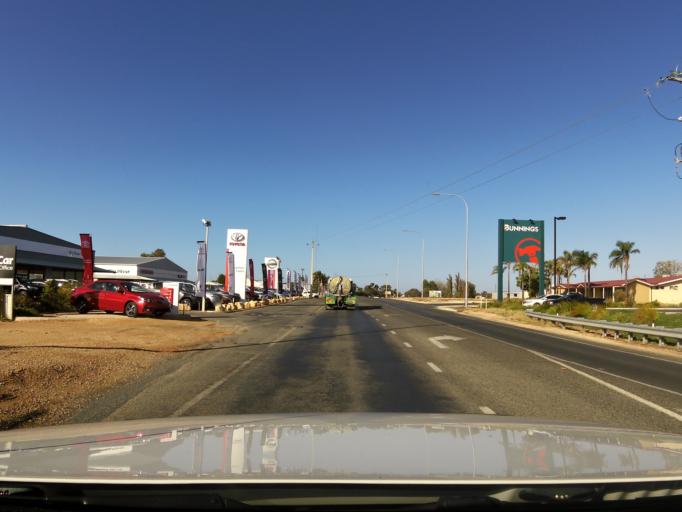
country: AU
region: South Australia
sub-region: Berri and Barmera
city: Berri
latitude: -34.2603
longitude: 140.6144
